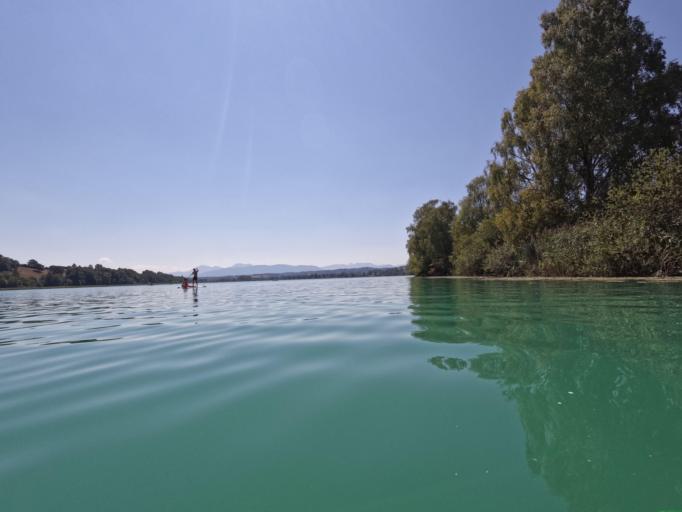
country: DE
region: Bavaria
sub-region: Upper Bavaria
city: Taching am See
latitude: 47.9697
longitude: 12.7401
